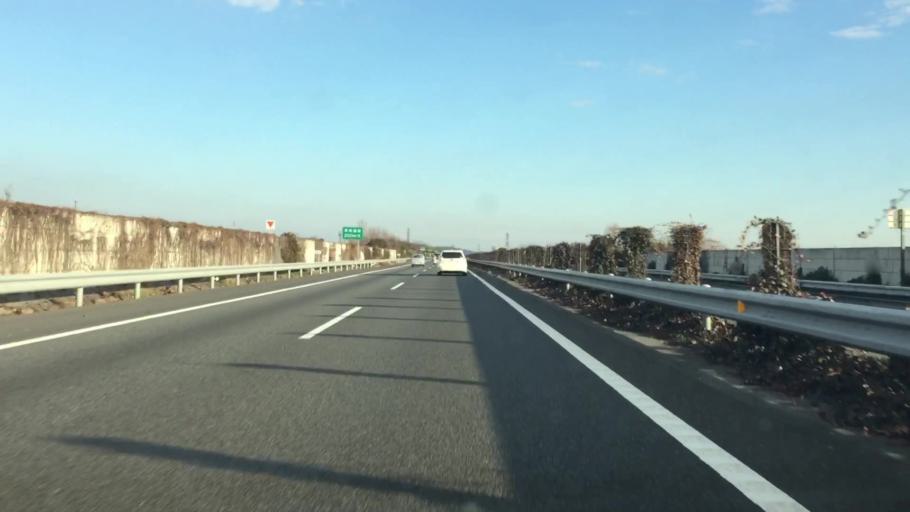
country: JP
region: Gunma
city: Isesaki
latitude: 36.3513
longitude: 139.2340
